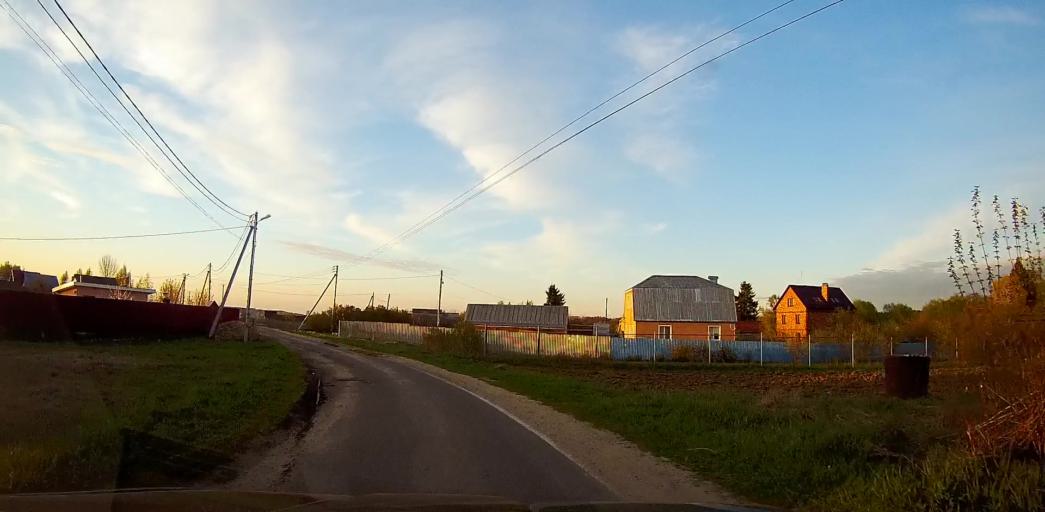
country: RU
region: Moskovskaya
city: Peski
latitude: 55.2105
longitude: 38.7403
